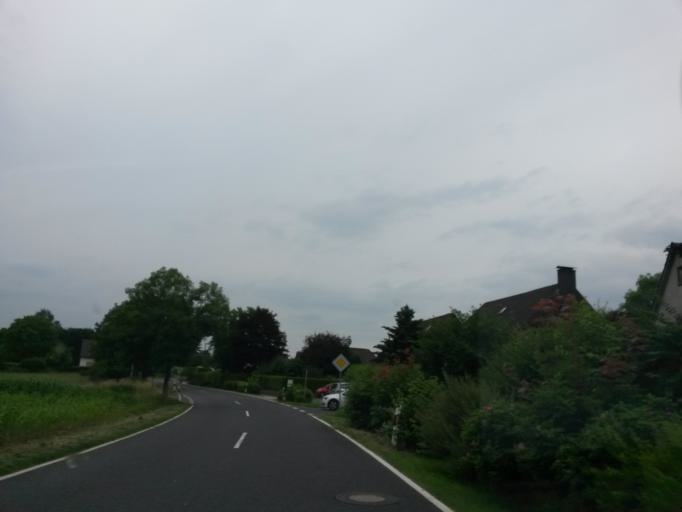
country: DE
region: North Rhine-Westphalia
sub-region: Regierungsbezirk Koln
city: Overath
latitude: 50.8779
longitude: 7.3183
